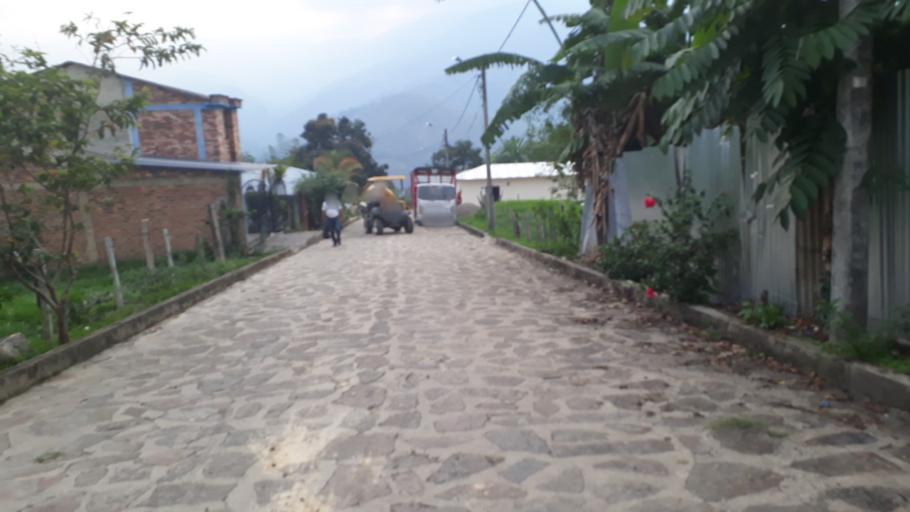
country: CO
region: Casanare
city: Nunchia
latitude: 5.6240
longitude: -72.4241
